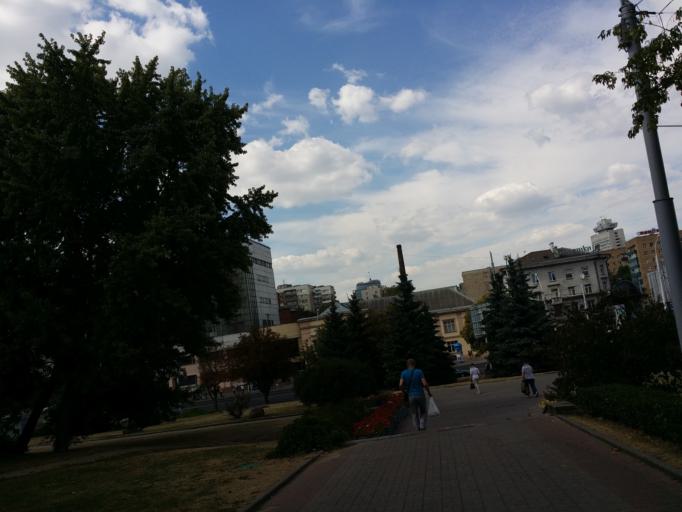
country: BY
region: Minsk
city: Minsk
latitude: 53.9010
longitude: 27.5493
